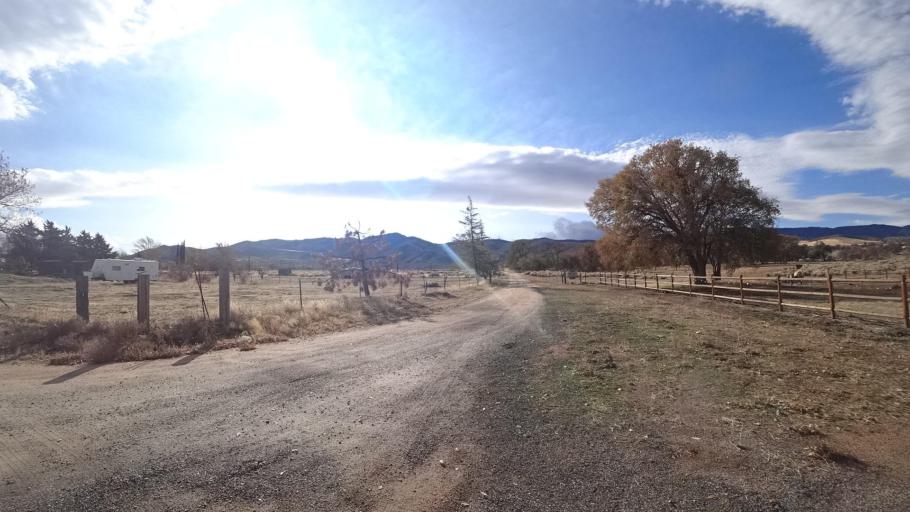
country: US
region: California
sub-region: Kern County
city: Golden Hills
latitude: 35.1168
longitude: -118.5082
